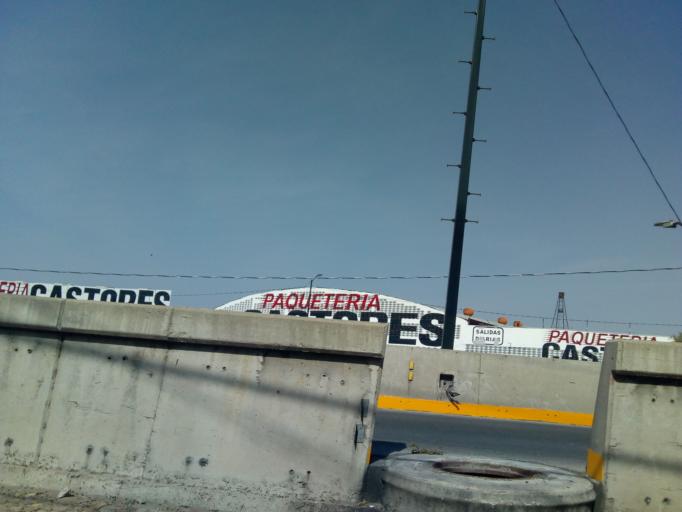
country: MX
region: Guanajuato
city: Leon
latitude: 21.1383
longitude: -101.6798
